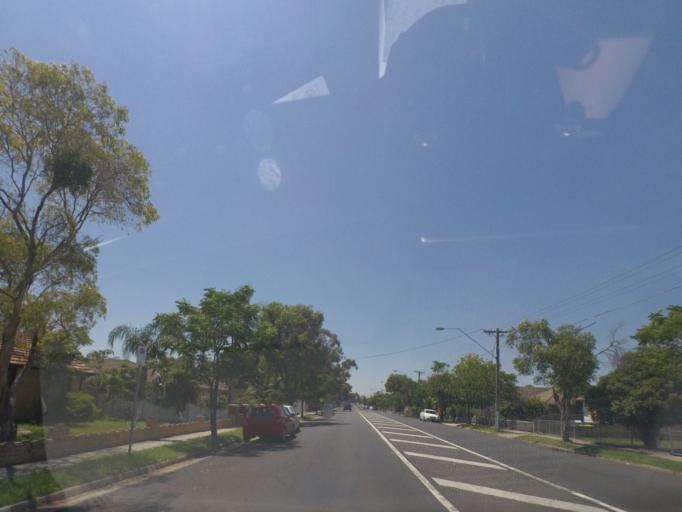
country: AU
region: Victoria
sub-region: Moreland
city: Pascoe Vale
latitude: -37.7237
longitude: 144.9397
